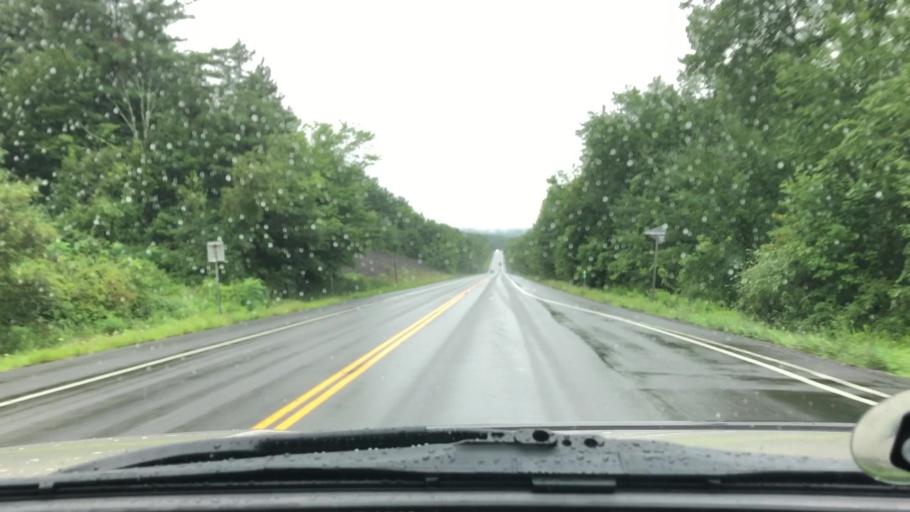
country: US
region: New York
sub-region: Greene County
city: Cairo
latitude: 42.3089
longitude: -74.0544
